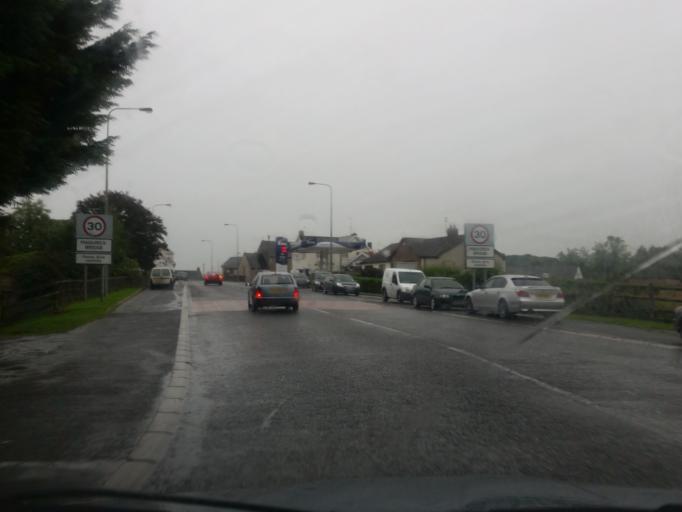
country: GB
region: Northern Ireland
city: Lisnaskea
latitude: 54.2973
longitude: -7.4670
